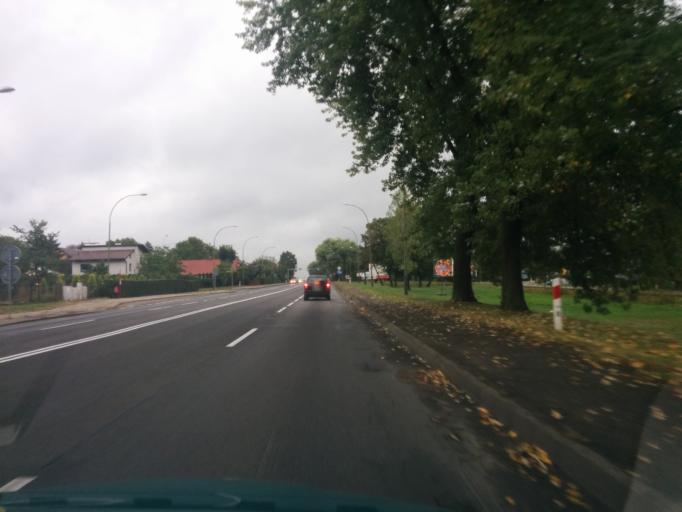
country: PL
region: Subcarpathian Voivodeship
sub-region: Powiat sanocki
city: Sanok
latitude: 49.5667
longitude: 22.1728
